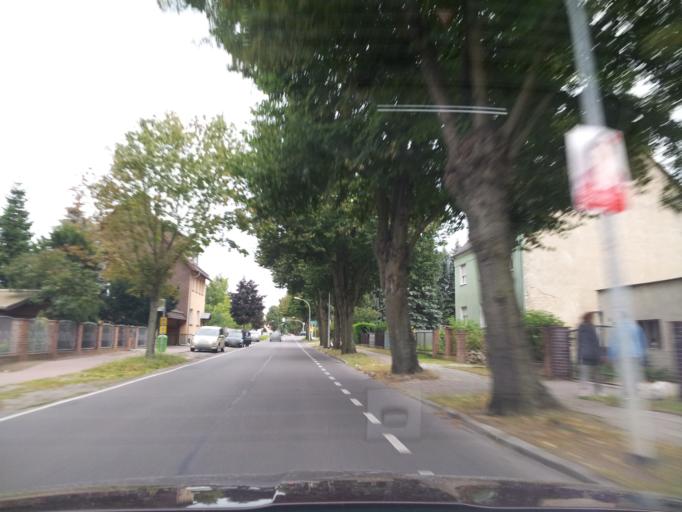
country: DE
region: Brandenburg
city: Luckenwalde
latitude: 52.0975
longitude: 13.1521
